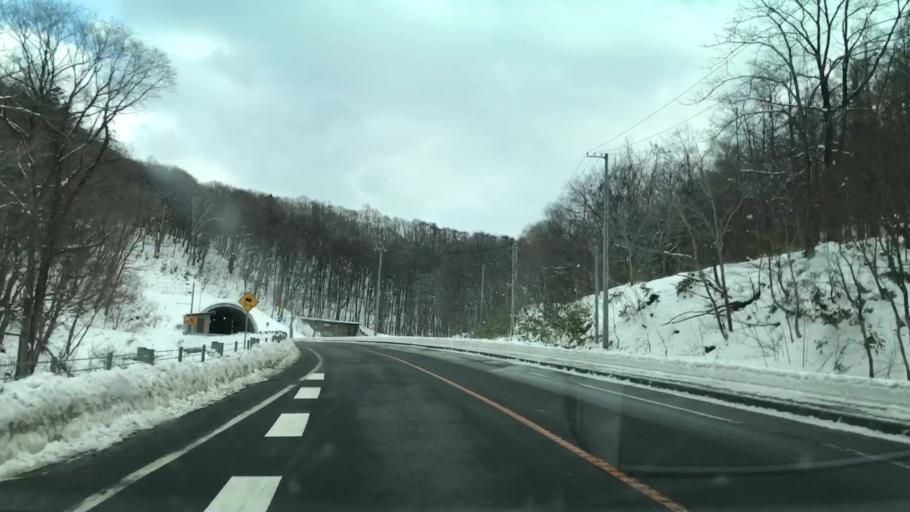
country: JP
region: Hokkaido
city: Yoichi
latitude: 43.2226
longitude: 140.7358
